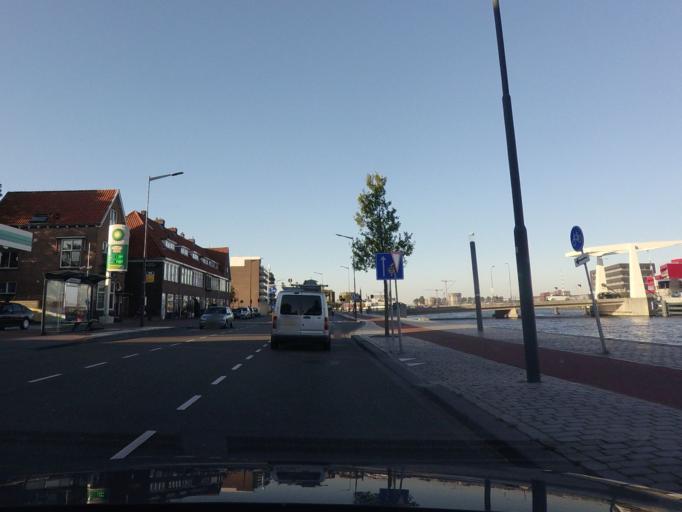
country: NL
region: North Holland
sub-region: Gemeente Haarlem
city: Haarlem
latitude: 52.3945
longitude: 4.6504
